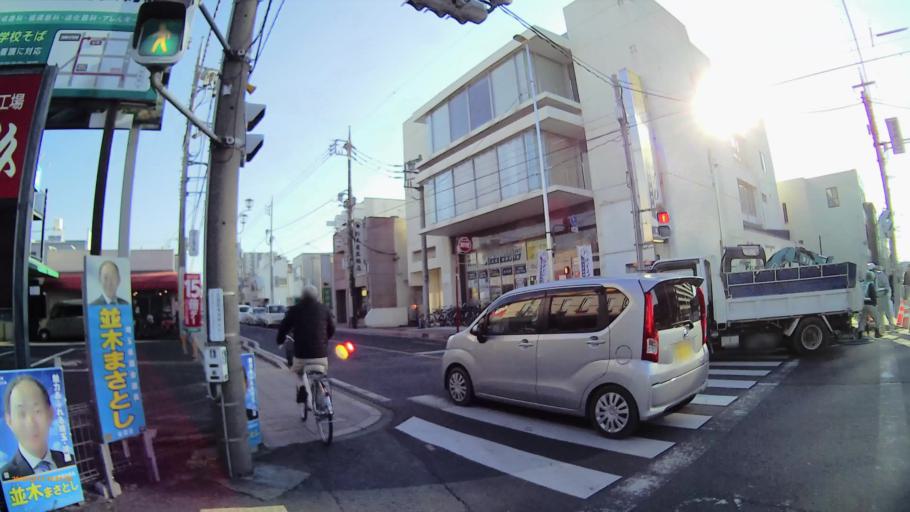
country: JP
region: Saitama
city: Konosu
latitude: 36.0602
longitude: 139.5126
